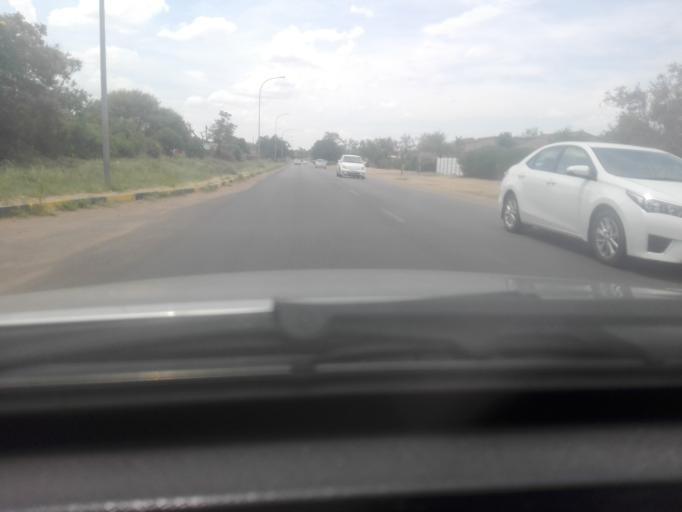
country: BW
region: South East
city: Gaborone
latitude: -24.6255
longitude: 25.9434
